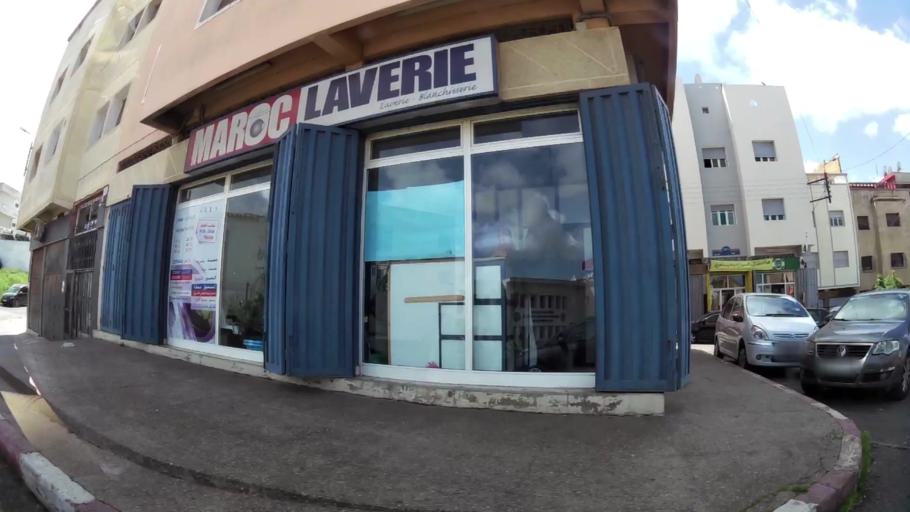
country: MA
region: Grand Casablanca
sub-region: Casablanca
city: Casablanca
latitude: 33.5410
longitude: -7.5922
